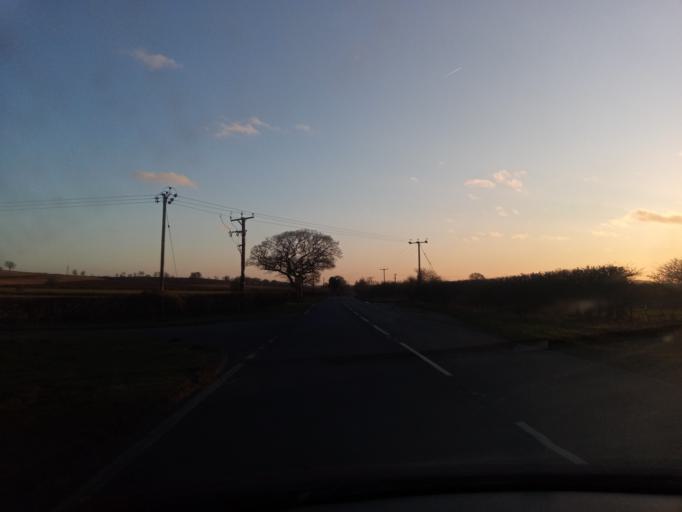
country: GB
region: England
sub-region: Nottinghamshire
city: Farnsfield
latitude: 53.0806
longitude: -1.0689
